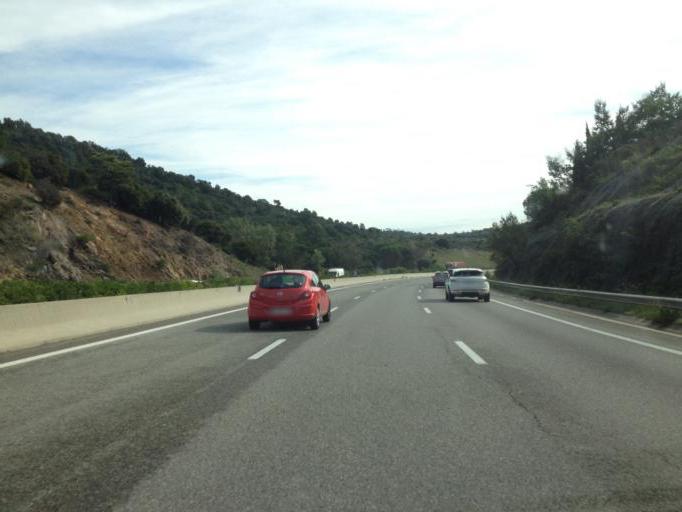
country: FR
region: Provence-Alpes-Cote d'Azur
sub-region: Departement du Var
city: Tanneron
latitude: 43.5390
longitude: 6.8484
